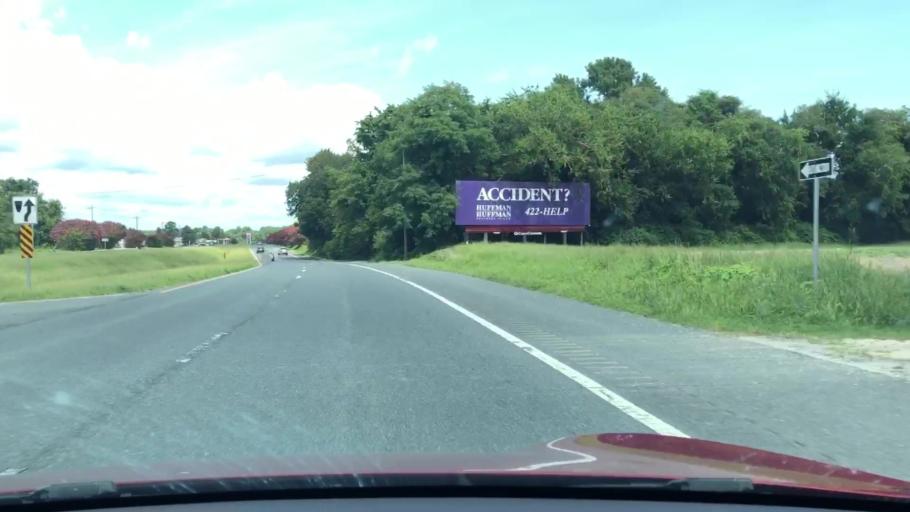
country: US
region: Virginia
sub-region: Northampton County
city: Cape Charles
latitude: 37.2990
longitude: -75.9690
